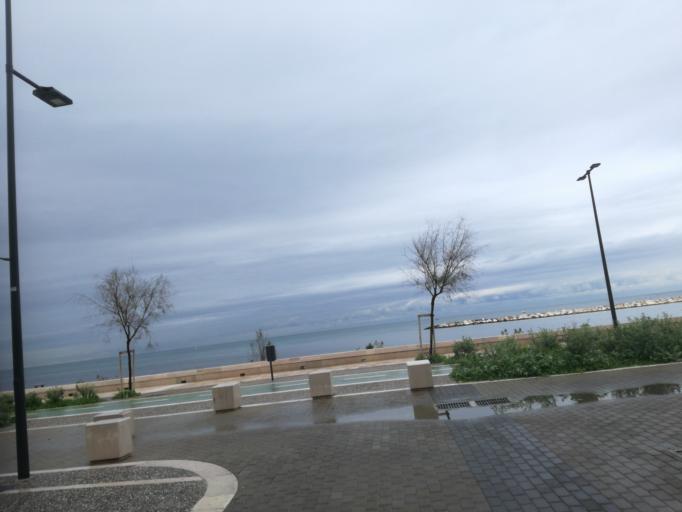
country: IT
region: Apulia
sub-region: Provincia di Bari
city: San Paolo
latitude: 41.1394
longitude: 16.8156
